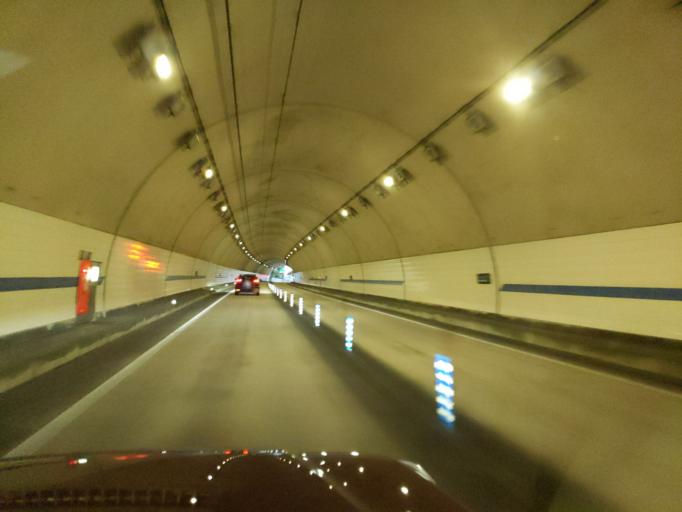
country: JP
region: Tokushima
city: Anan
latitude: 33.7711
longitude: 134.5750
